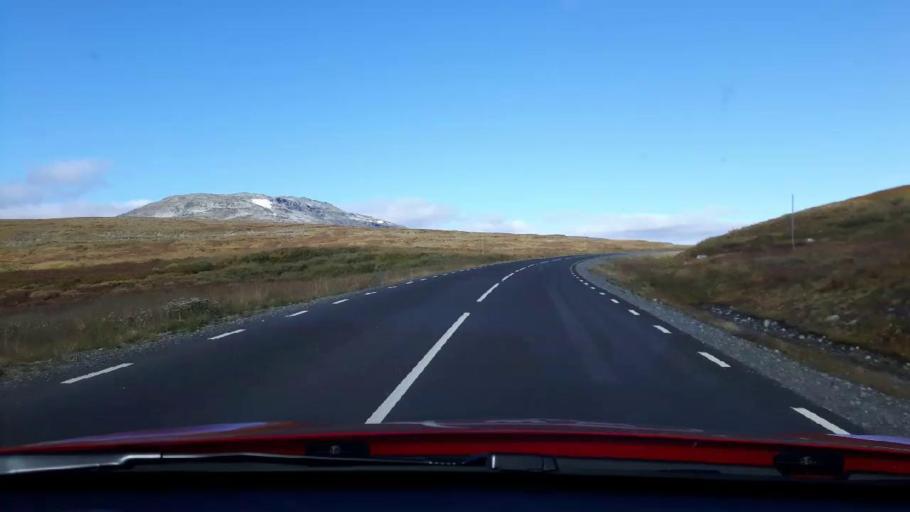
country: NO
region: Nordland
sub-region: Hattfjelldal
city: Hattfjelldal
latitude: 65.0365
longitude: 14.3289
